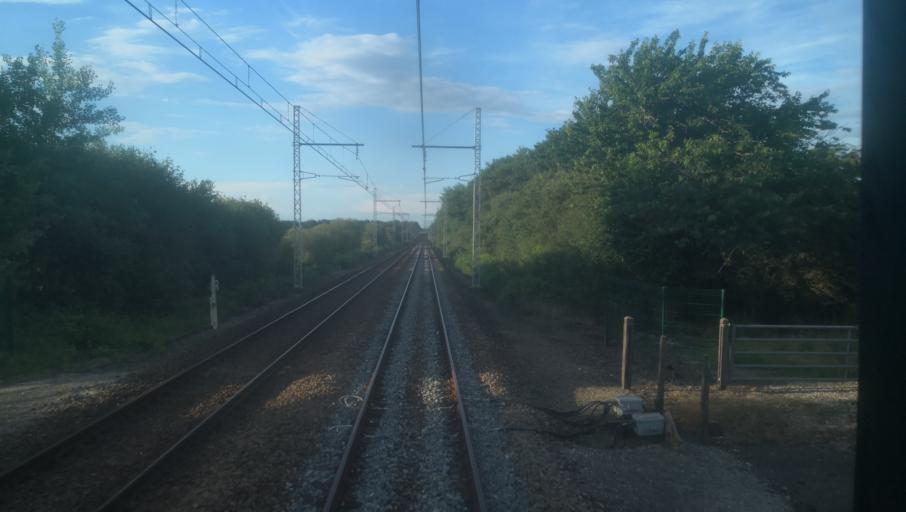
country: FR
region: Centre
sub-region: Departement de l'Indre
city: Luant
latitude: 46.7073
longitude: 1.5716
